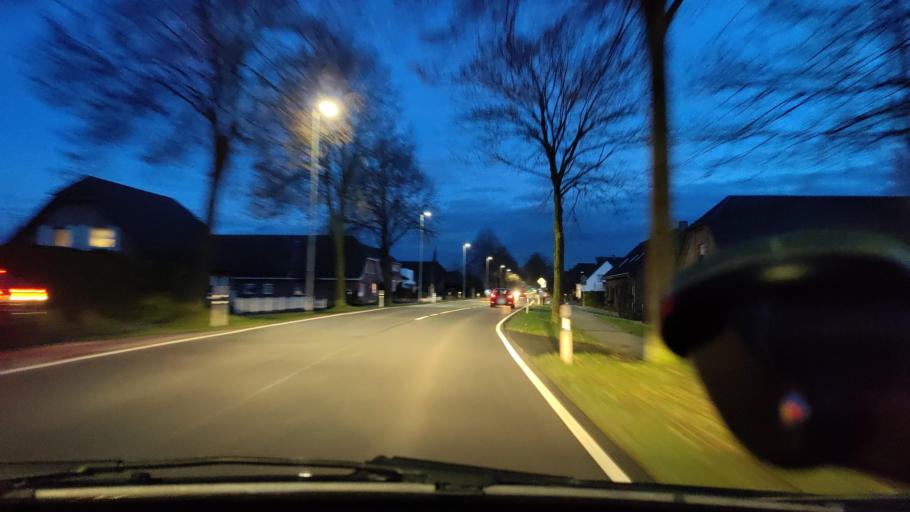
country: DE
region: North Rhine-Westphalia
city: Rees
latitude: 51.7032
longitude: 6.3687
